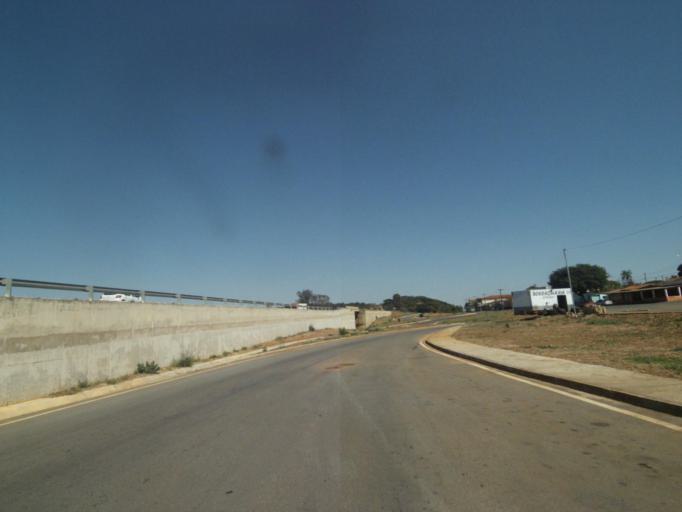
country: BR
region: Goias
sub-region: Anapolis
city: Anapolis
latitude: -16.1908
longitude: -49.0342
